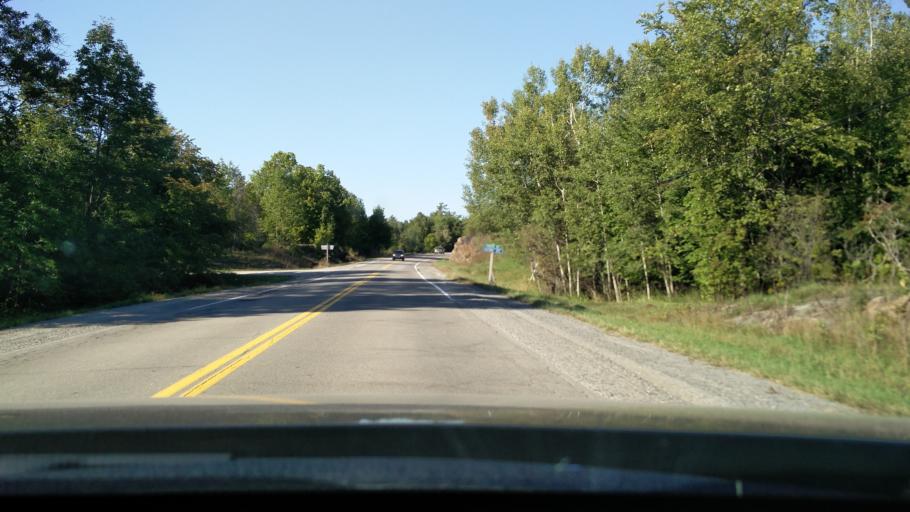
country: CA
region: Ontario
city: Perth
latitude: 44.7159
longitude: -76.4014
